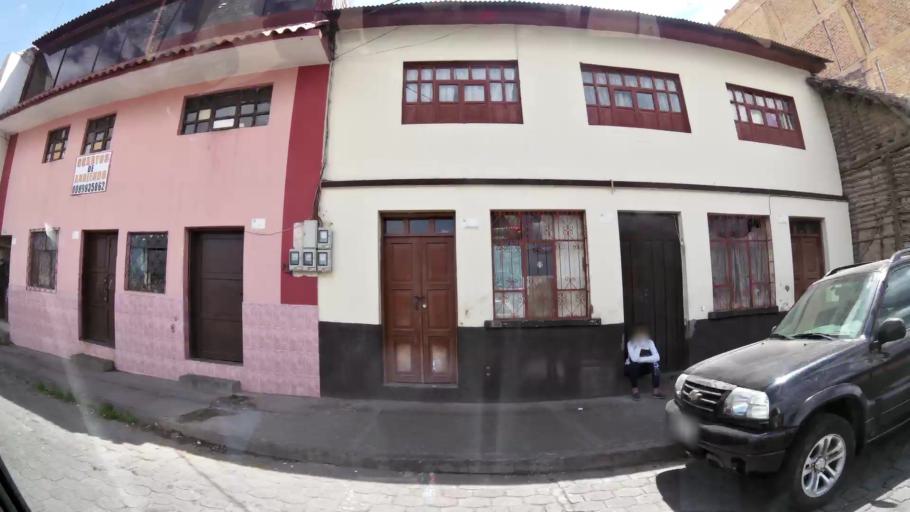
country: EC
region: Tungurahua
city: Ambato
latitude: -1.2473
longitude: -78.6300
